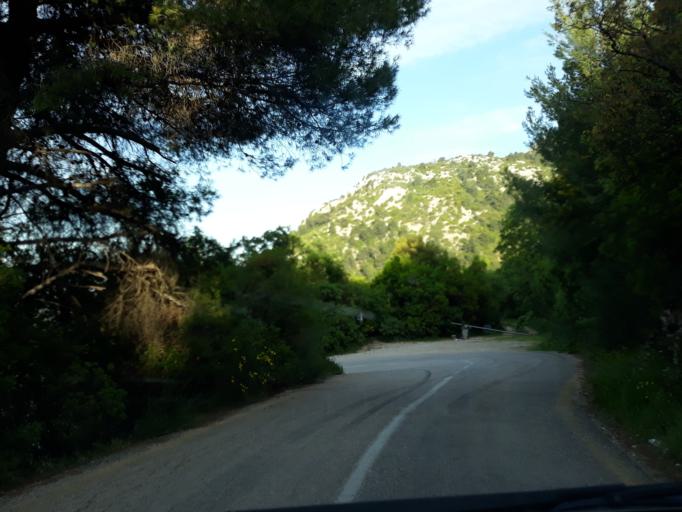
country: GR
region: Attica
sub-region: Nomarchia Anatolikis Attikis
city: Afidnes
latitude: 38.2265
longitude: 23.7963
